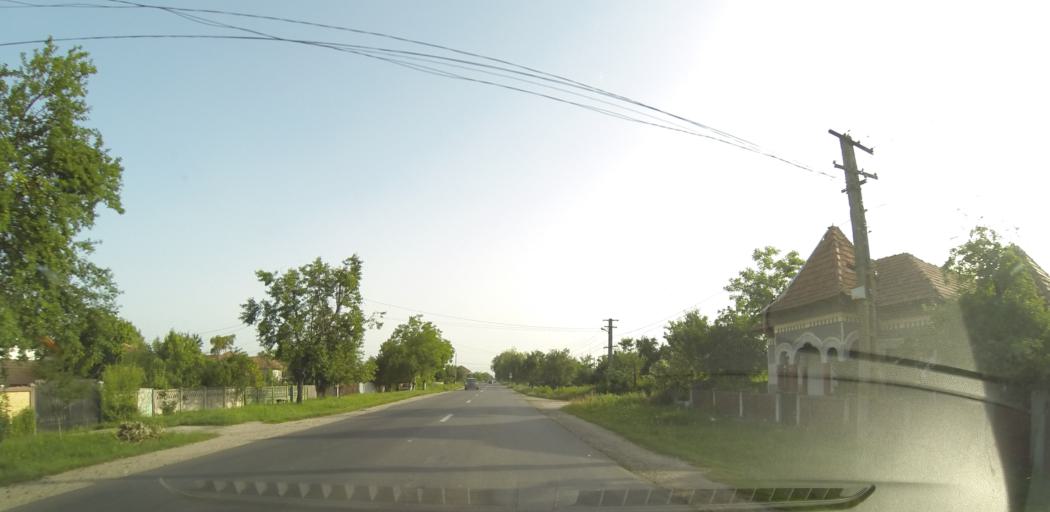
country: RO
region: Valcea
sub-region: Comuna Babeni
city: Valea Mare
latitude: 44.9036
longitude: 24.2335
